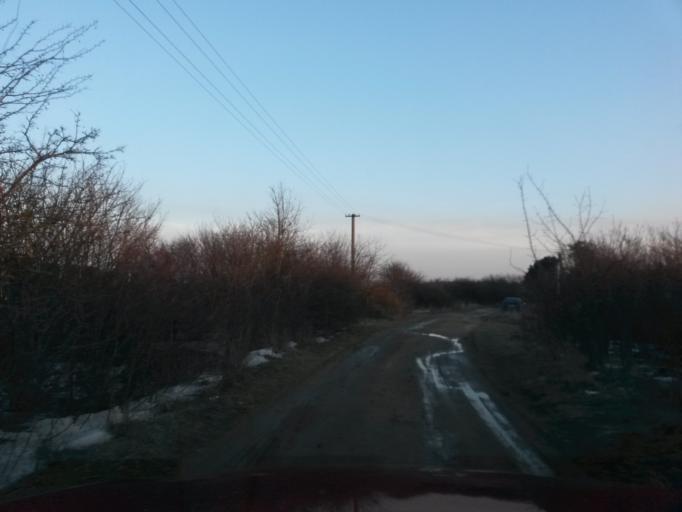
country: SK
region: Kosicky
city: Kosice
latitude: 48.7261
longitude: 21.2198
